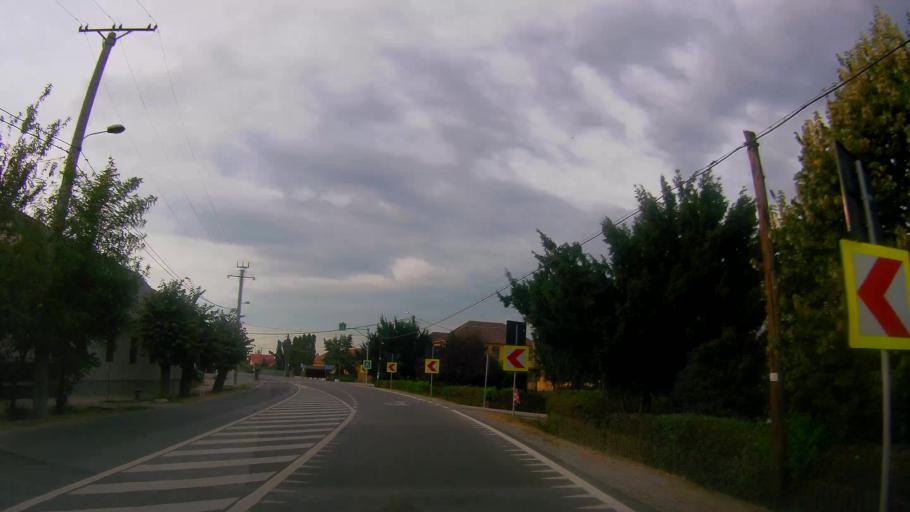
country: RO
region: Satu Mare
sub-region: Comuna Turulung
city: Turulung
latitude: 47.9314
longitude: 23.0839
